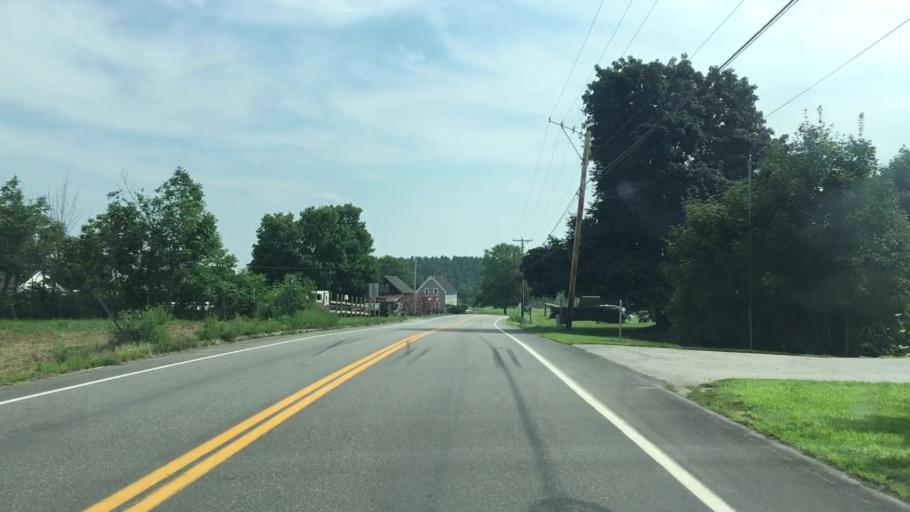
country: US
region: Maine
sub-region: Kennebec County
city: Windsor
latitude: 44.3079
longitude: -69.5806
